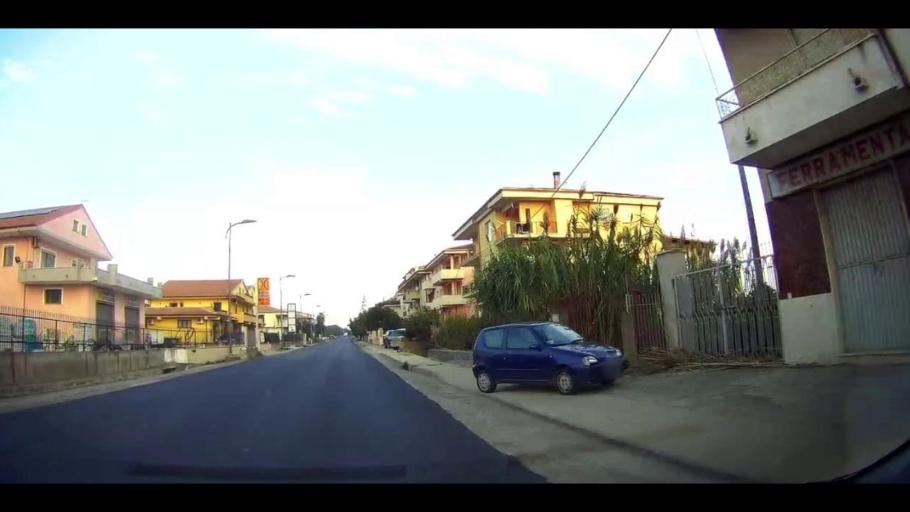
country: IT
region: Calabria
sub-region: Provincia di Crotone
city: Torretta
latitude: 39.4566
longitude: 17.0329
